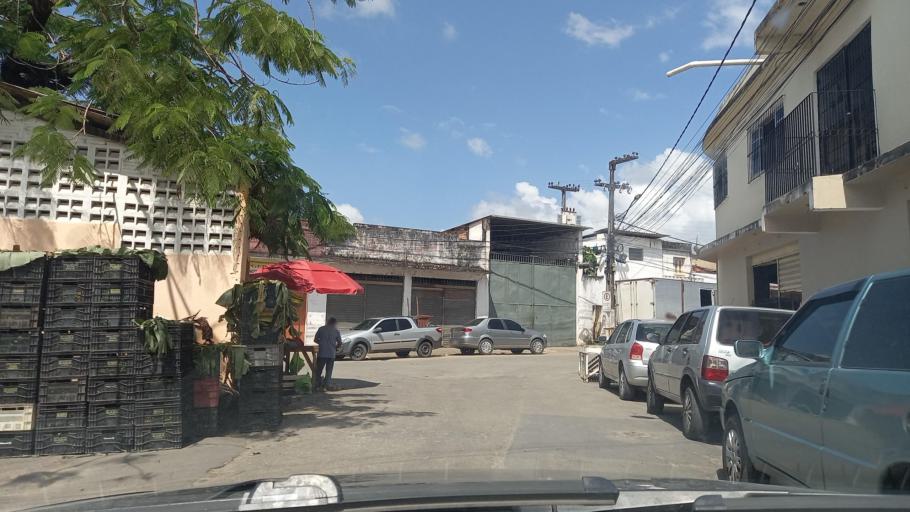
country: BR
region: Pernambuco
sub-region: Goiana
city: Goiana
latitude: -7.5583
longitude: -35.0004
